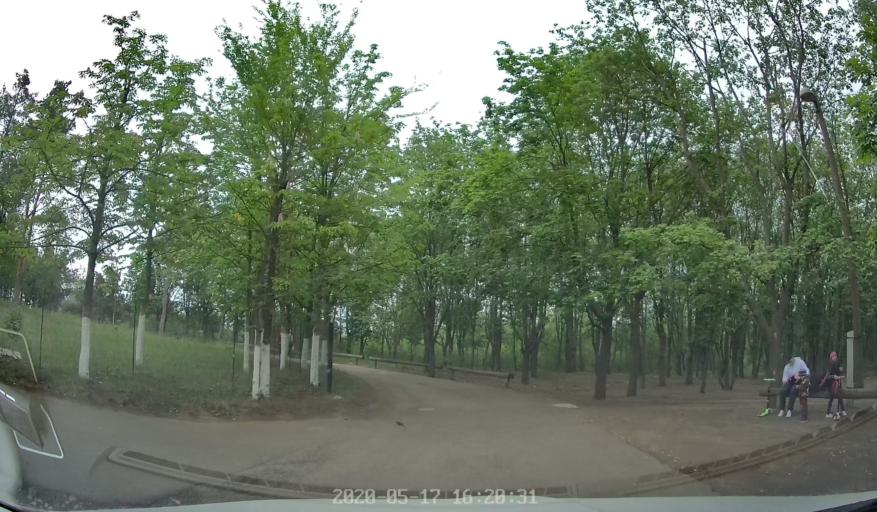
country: MD
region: Chisinau
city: Chisinau
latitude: 46.9726
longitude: 28.8745
